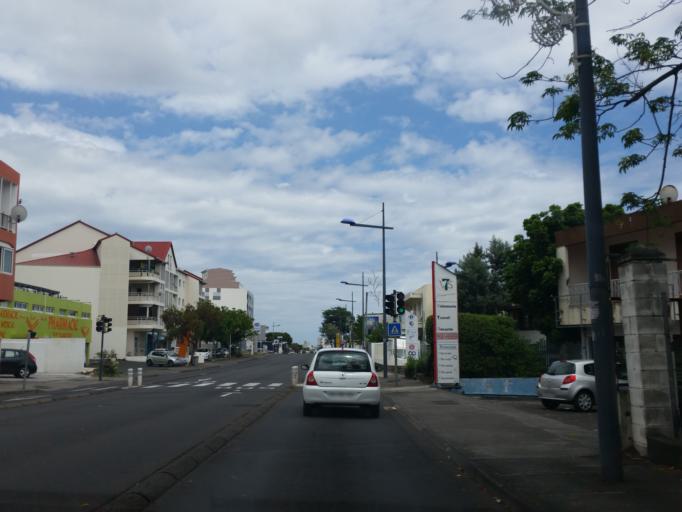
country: RE
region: Reunion
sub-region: Reunion
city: Saint-Denis
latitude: -20.8906
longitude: 55.4792
